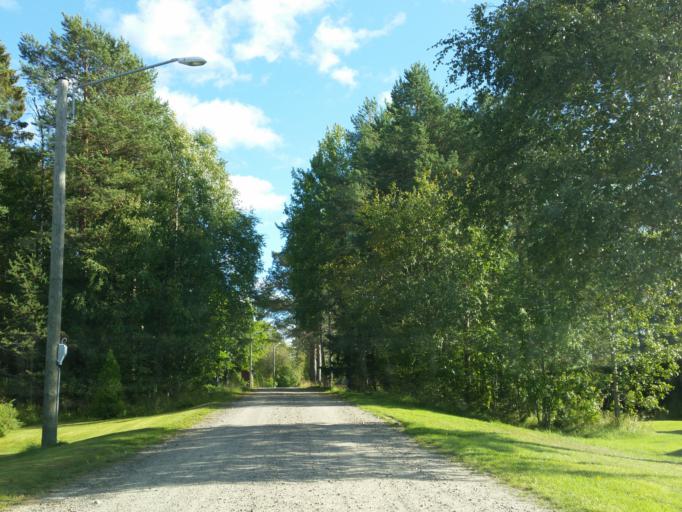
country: SE
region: Vaesterbotten
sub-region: Robertsfors Kommun
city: Robertsfors
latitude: 64.1603
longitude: 20.9568
